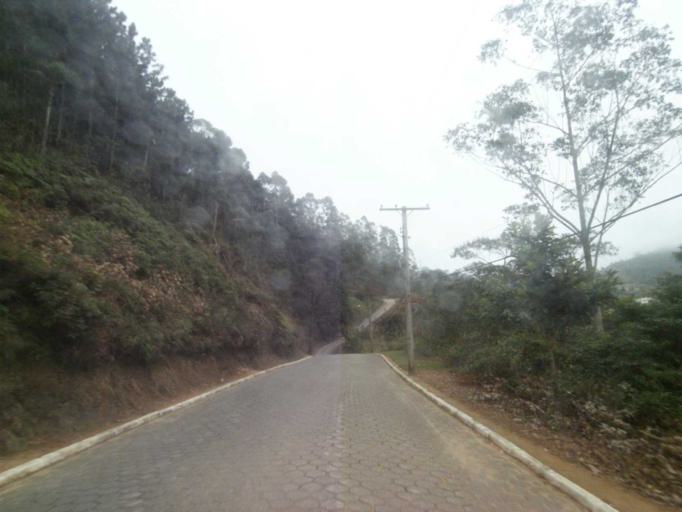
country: BR
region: Santa Catarina
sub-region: Anitapolis
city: Anitapolis
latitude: -27.9075
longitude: -49.1314
